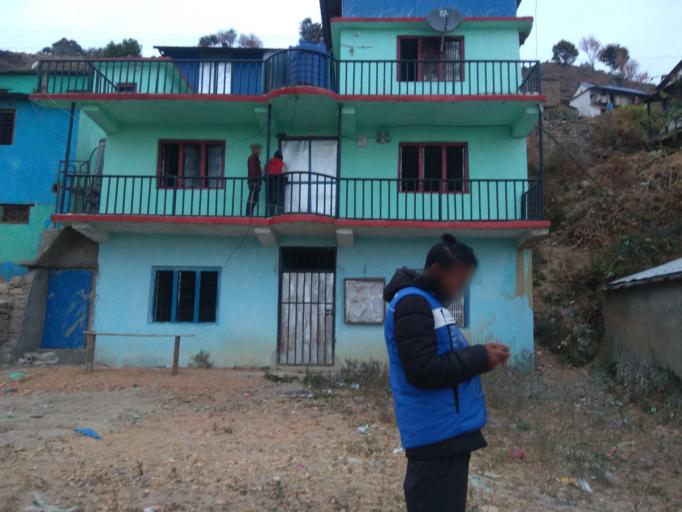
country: NP
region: Far Western
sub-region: Seti Zone
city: Achham
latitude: 29.2584
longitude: 81.6210
